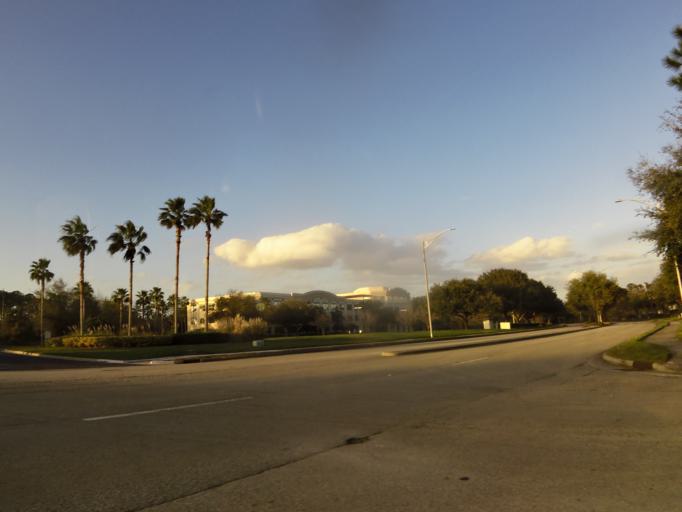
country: US
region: Florida
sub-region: Duval County
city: Jacksonville Beach
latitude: 30.2580
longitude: -81.4626
